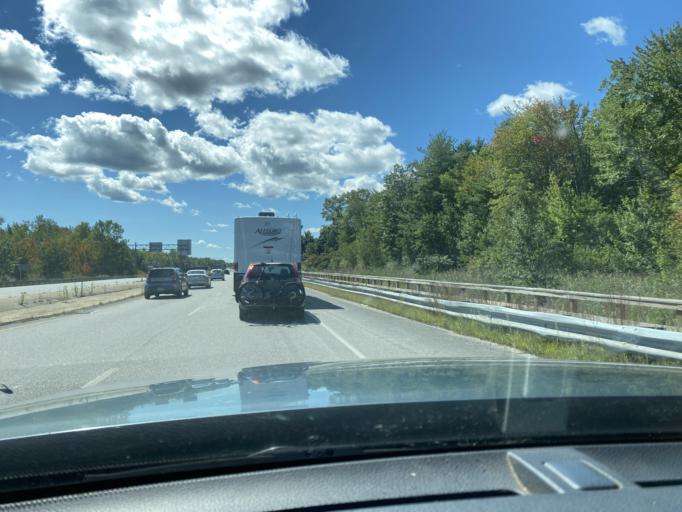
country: US
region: New Hampshire
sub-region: Rockingham County
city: Greenland
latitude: 43.0558
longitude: -70.8112
